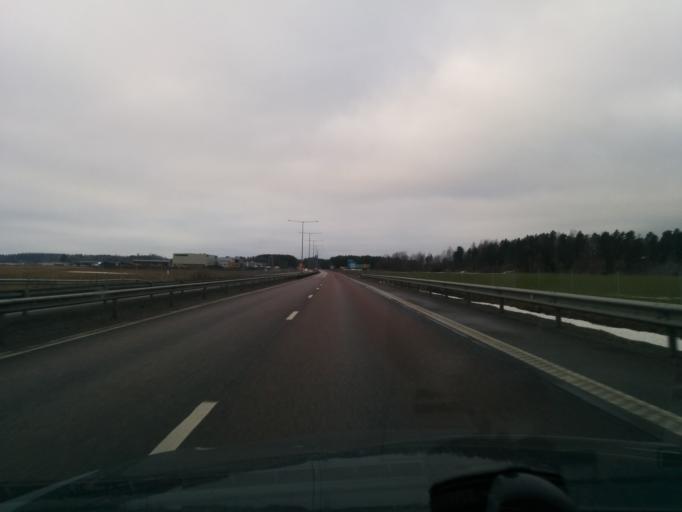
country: SE
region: Vaestmanland
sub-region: Vasteras
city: Tillberga
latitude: 59.6150
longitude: 16.6452
